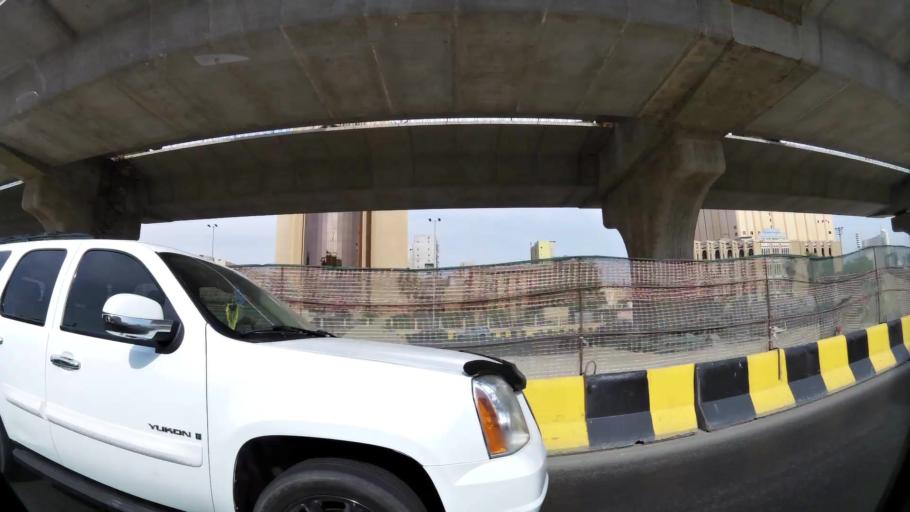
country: KW
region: Al Asimah
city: Ash Shamiyah
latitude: 29.3473
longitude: 47.9384
